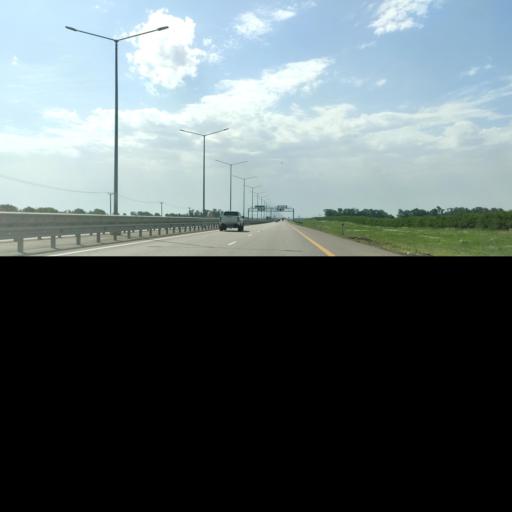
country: RU
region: Voronezj
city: Podkletnoye
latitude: 51.5672
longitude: 39.4749
